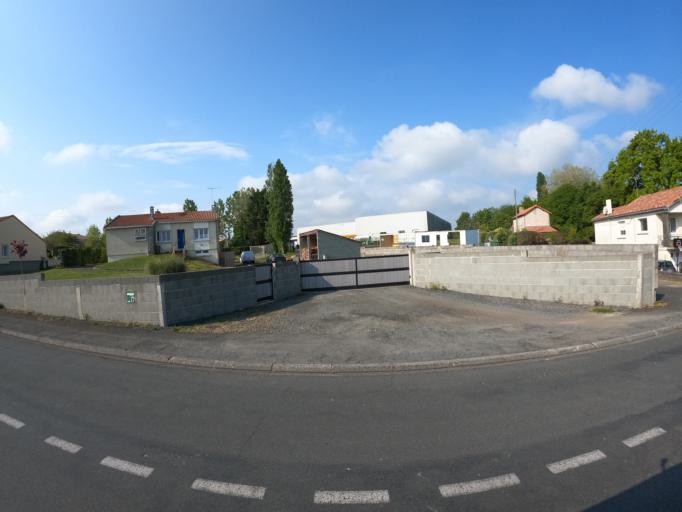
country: FR
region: Pays de la Loire
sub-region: Departement de Maine-et-Loire
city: La Romagne
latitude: 47.0621
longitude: -1.0252
